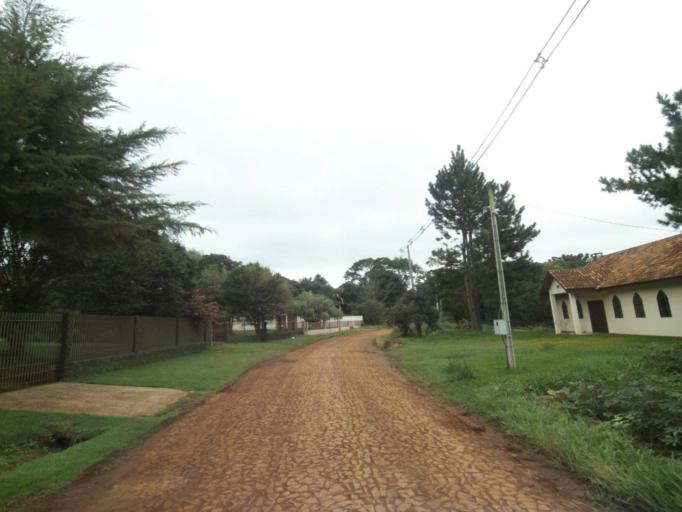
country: BR
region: Parana
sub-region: Pitanga
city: Pitanga
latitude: -24.9298
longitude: -51.8707
